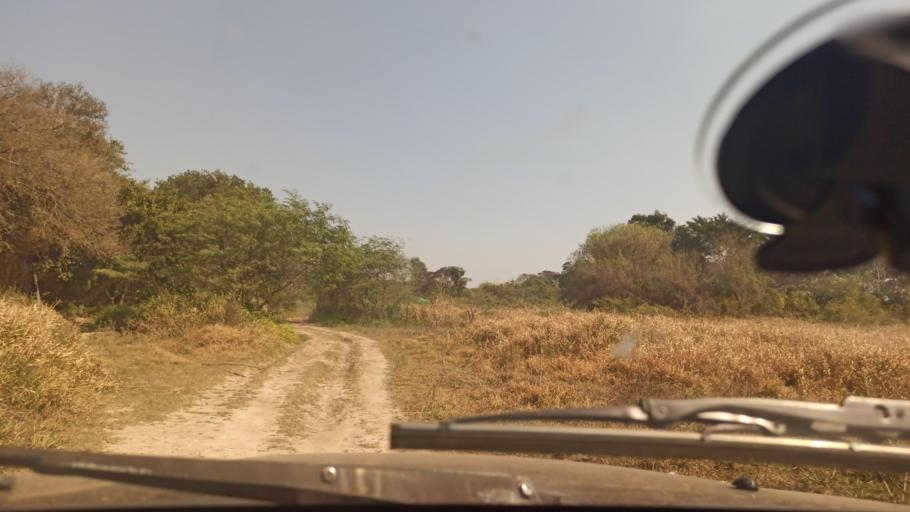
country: PY
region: Asuncion
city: Asuncion
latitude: -25.3298
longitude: -57.6825
